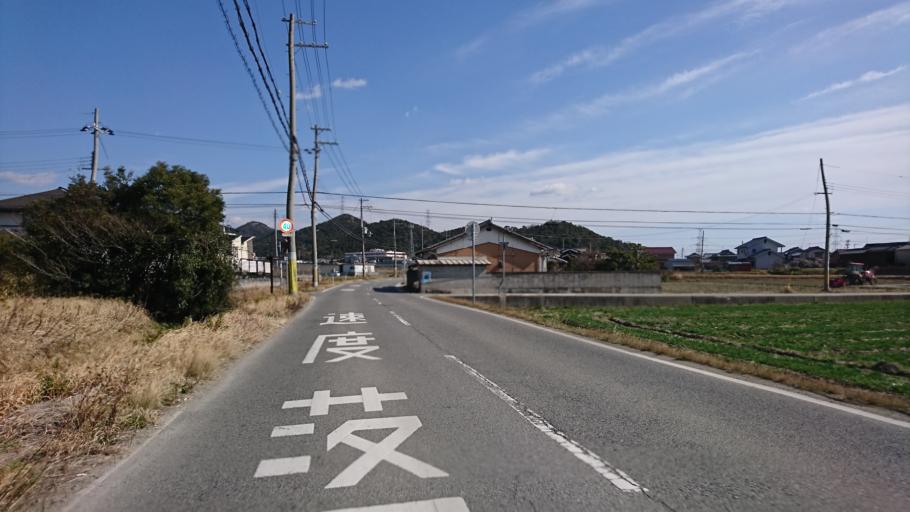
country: JP
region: Hyogo
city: Kakogawacho-honmachi
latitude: 34.8039
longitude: 134.8266
